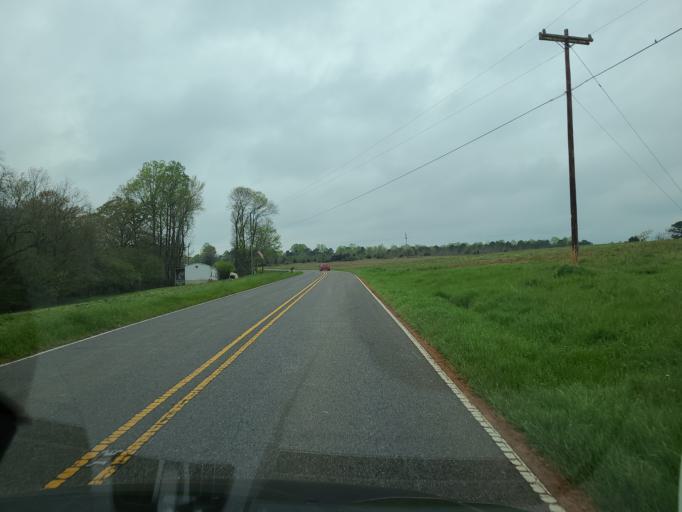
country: US
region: North Carolina
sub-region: Gaston County
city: Cherryville
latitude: 35.4281
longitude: -81.4779
